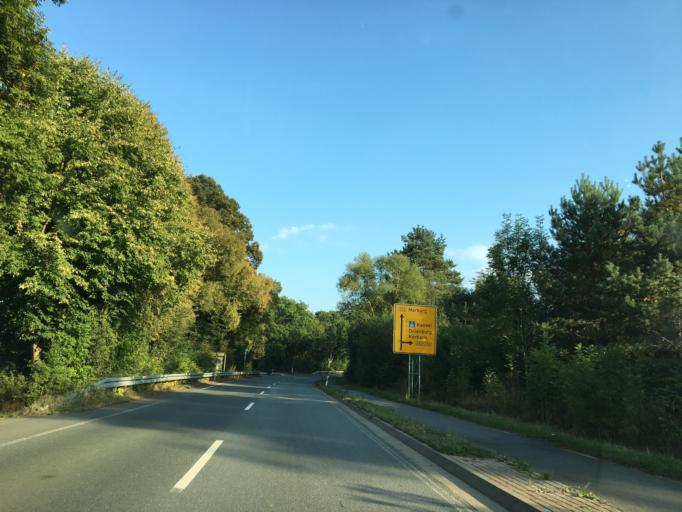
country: DE
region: Hesse
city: Frankenberg
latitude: 51.0464
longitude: 8.8051
